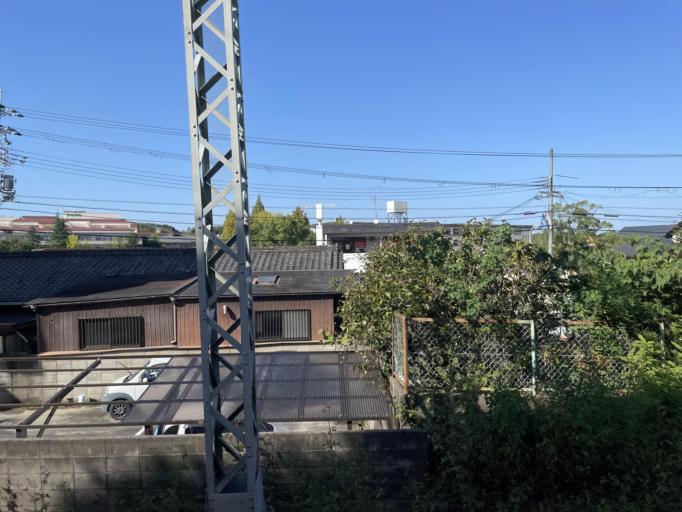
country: JP
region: Nara
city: Nara-shi
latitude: 34.6978
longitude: 135.7730
